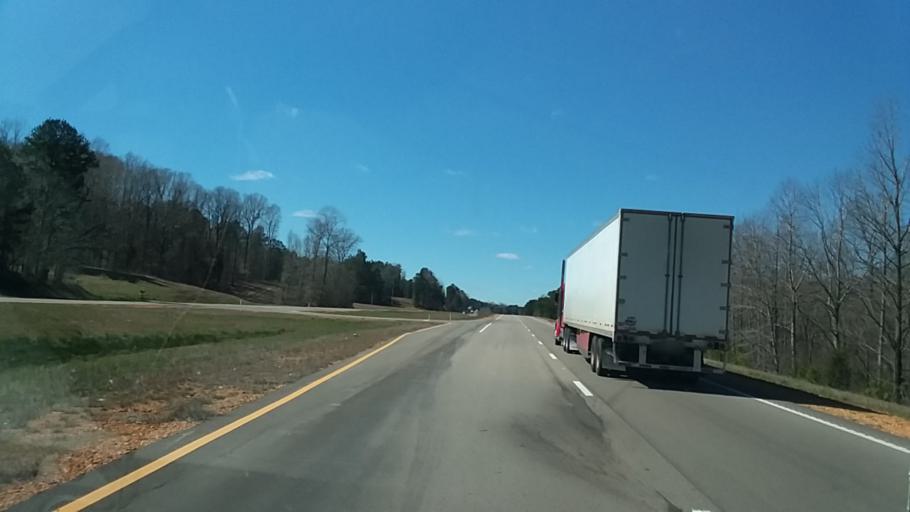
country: US
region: Mississippi
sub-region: Alcorn County
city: Farmington
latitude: 34.8598
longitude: -88.3997
